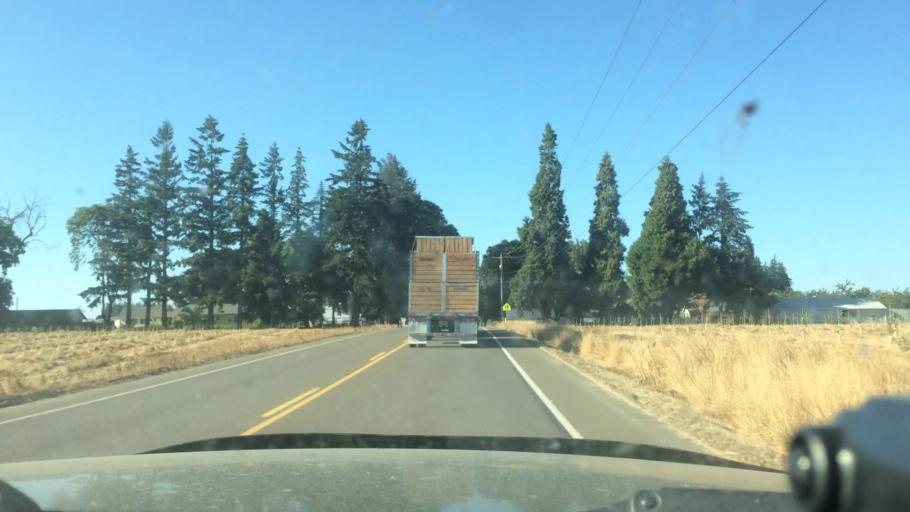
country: US
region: Oregon
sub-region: Marion County
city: Hayesville
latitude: 45.0677
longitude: -122.9801
